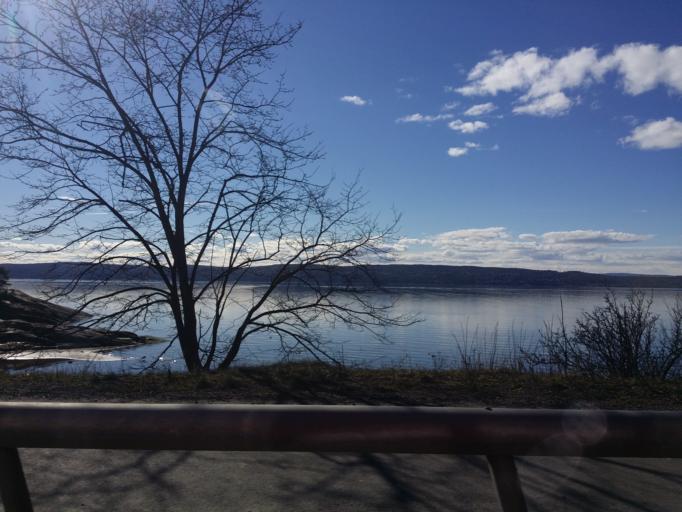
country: NO
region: Akershus
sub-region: Oppegard
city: Kolbotn
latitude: 59.8427
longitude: 10.7753
